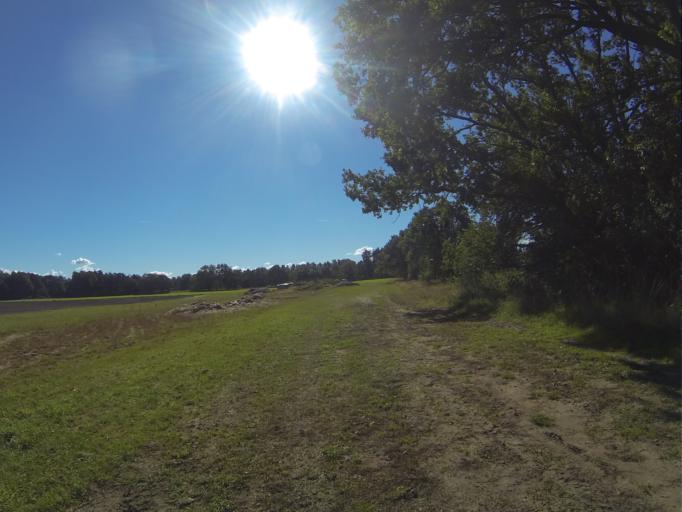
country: SE
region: Skane
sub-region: Hoors Kommun
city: Loberod
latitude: 55.7274
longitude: 13.4098
